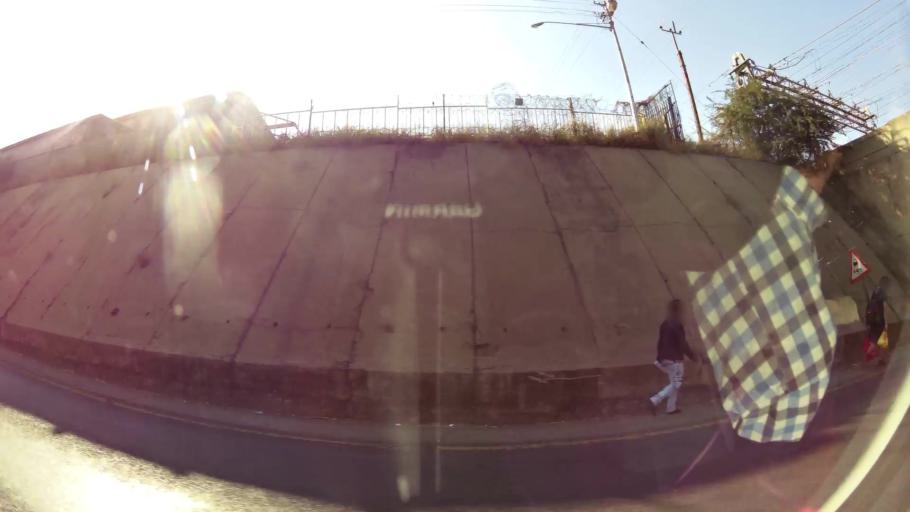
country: ZA
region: Gauteng
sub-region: City of Tshwane Metropolitan Municipality
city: Pretoria
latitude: -25.6781
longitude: 28.1825
